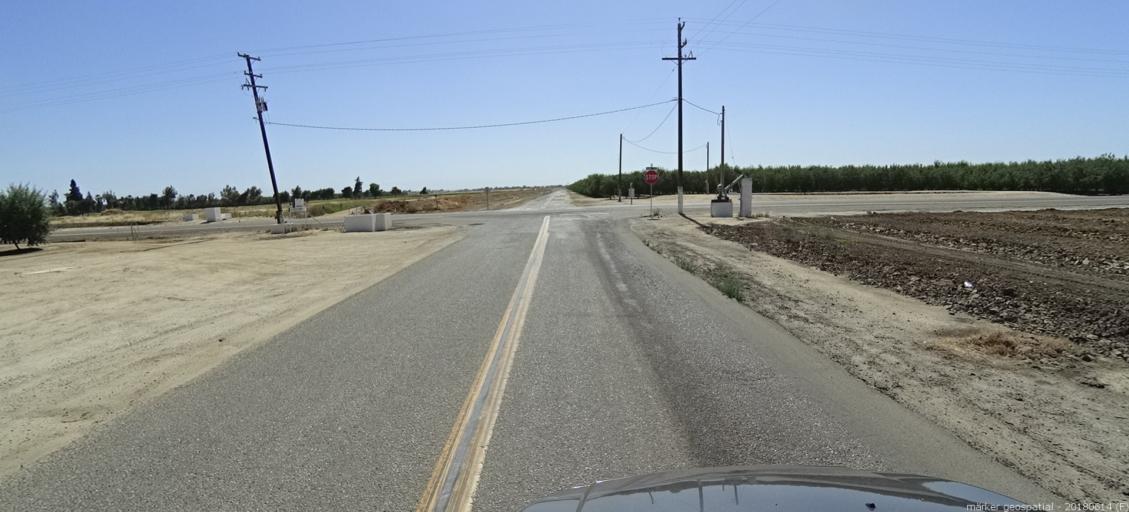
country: US
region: California
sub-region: Madera County
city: Madera
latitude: 36.9819
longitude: -120.1291
